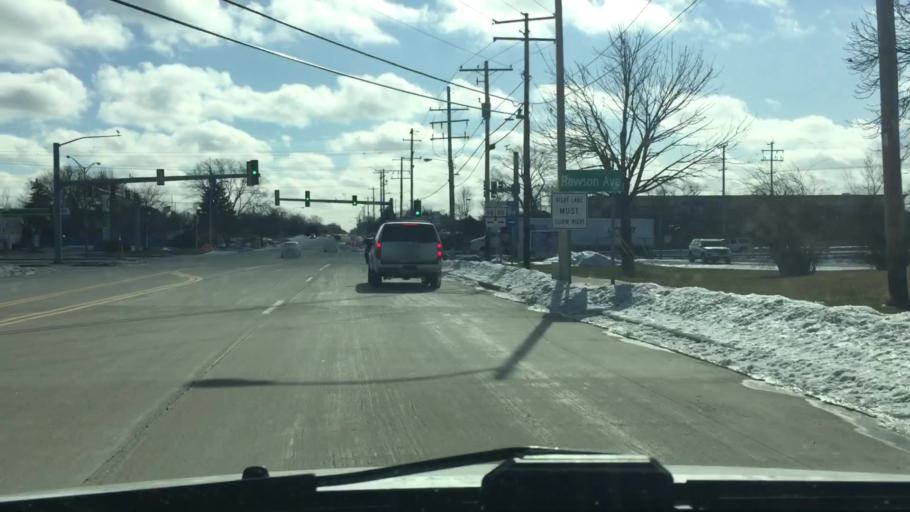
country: US
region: Wisconsin
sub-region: Milwaukee County
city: Greendale
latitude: 42.9170
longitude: -87.9308
